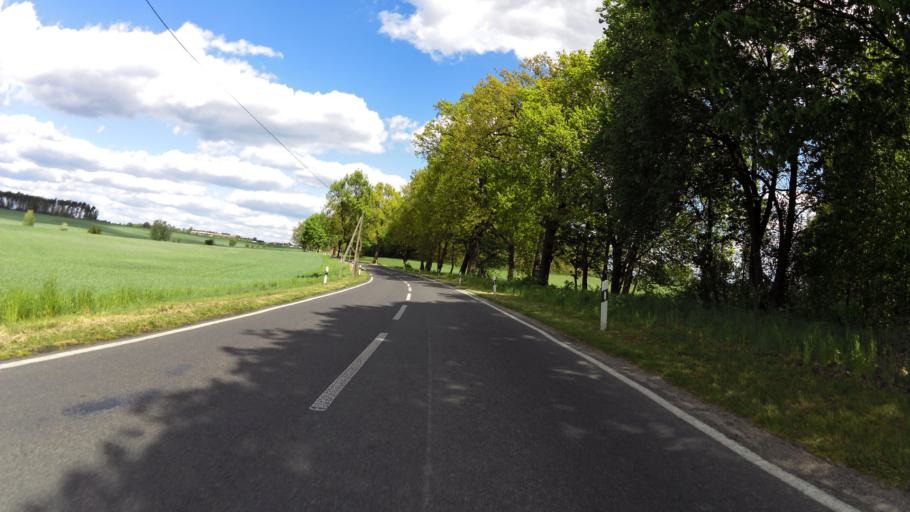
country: DE
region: Brandenburg
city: Diensdorf-Radlow
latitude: 52.1912
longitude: 14.1001
